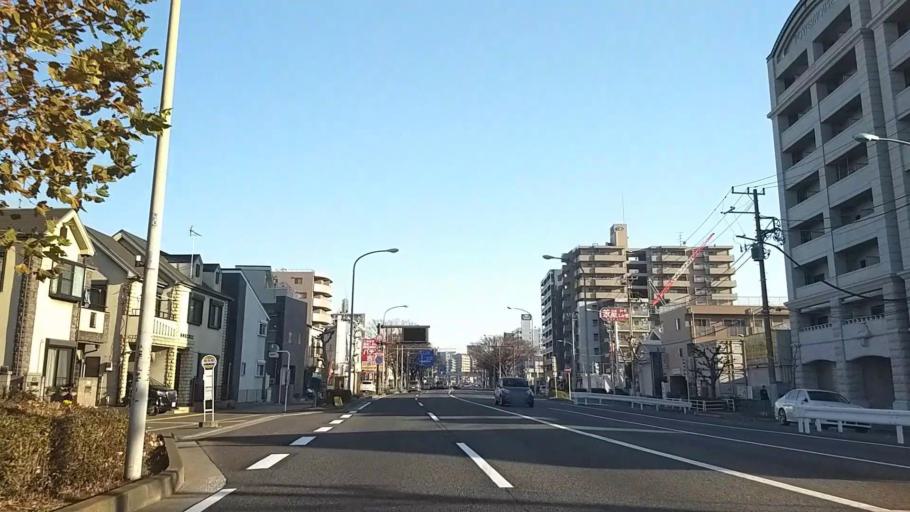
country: JP
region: Kanagawa
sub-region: Kawasaki-shi
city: Kawasaki
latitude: 35.5142
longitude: 139.6862
